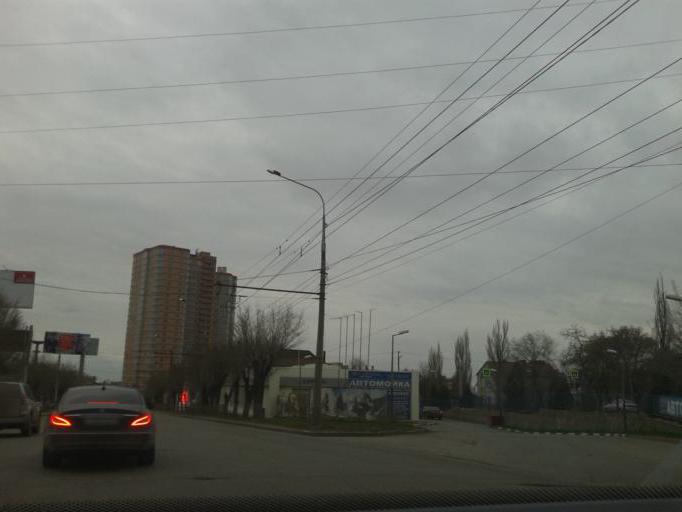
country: RU
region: Volgograd
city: Volgograd
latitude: 48.7241
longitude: 44.5016
